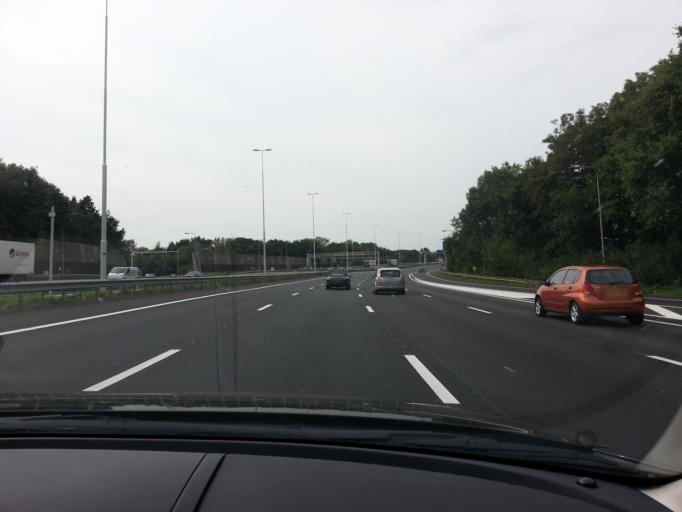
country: NL
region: South Holland
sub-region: Gemeente Zwijndrecht
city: Zwijndrecht
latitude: 51.8152
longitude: 4.6328
